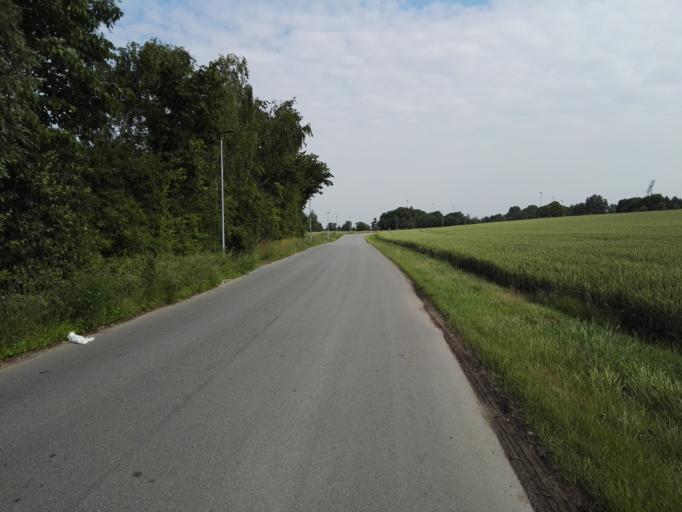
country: DK
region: Capital Region
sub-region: Egedal Kommune
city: Olstykke
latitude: 55.7784
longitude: 12.1414
